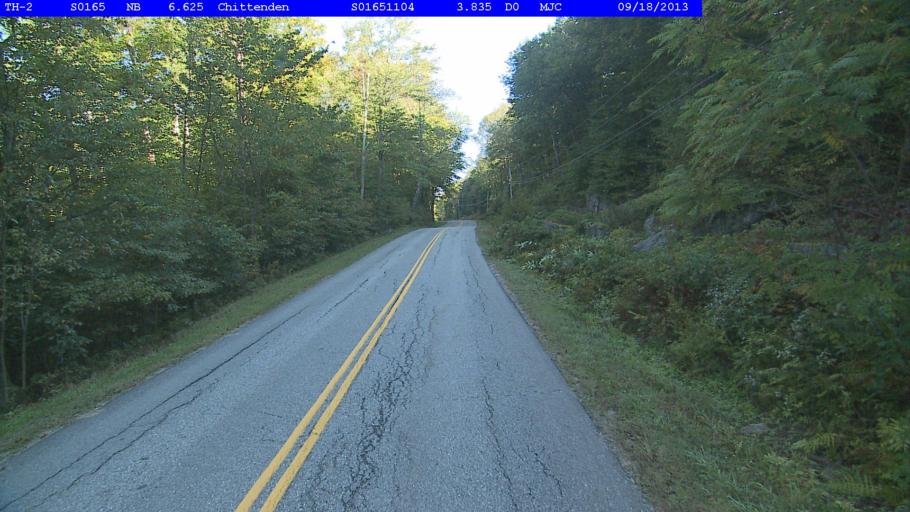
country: US
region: Vermont
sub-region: Rutland County
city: Rutland
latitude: 43.7292
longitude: -72.9708
